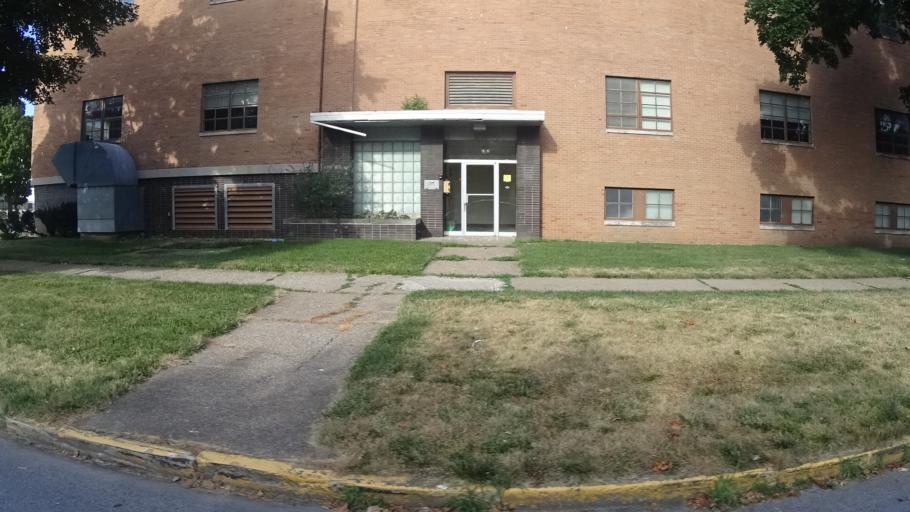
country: US
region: Ohio
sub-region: Erie County
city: Sandusky
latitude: 41.4534
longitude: -82.7082
